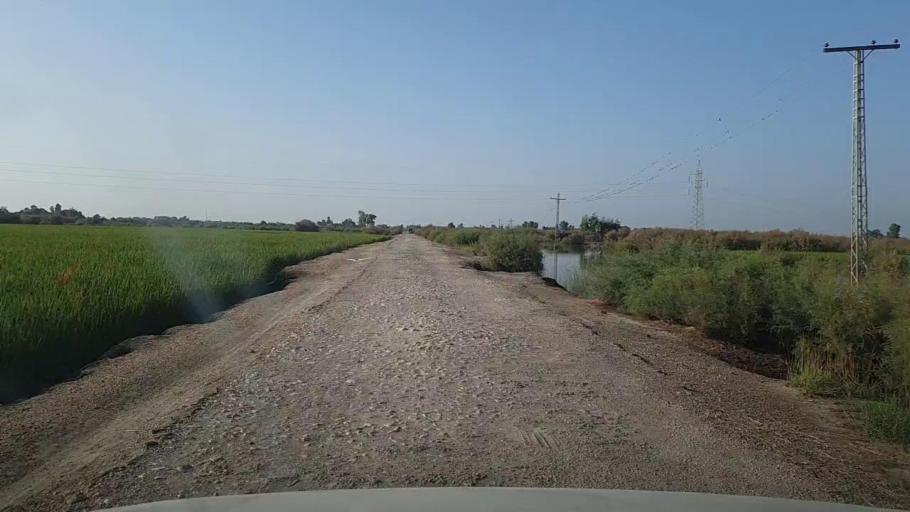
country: PK
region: Sindh
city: Kandhkot
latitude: 28.3072
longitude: 69.3284
